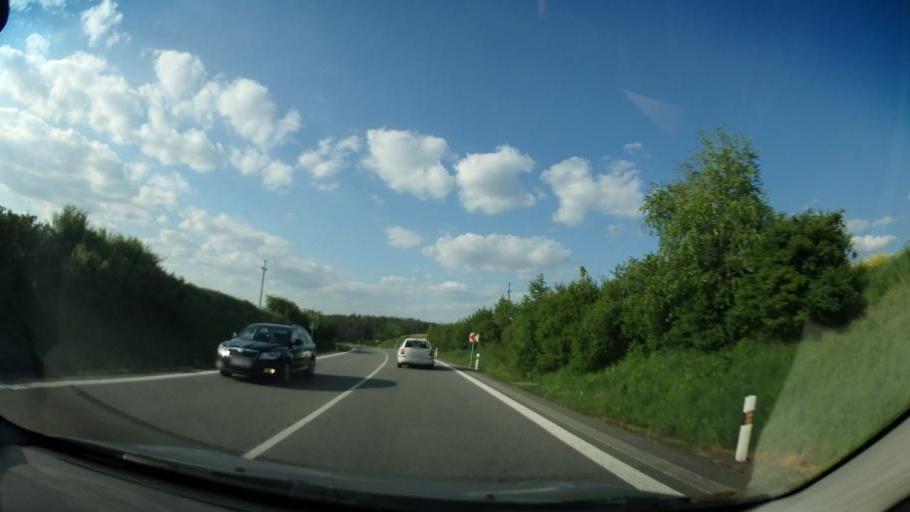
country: CZ
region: Vysocina
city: Budisov
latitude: 49.3151
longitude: 15.9712
